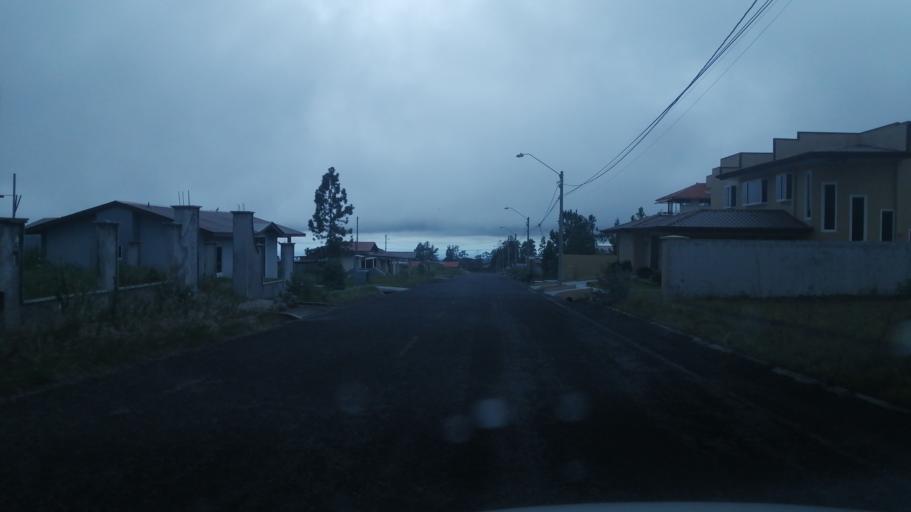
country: PA
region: Chiriqui
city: Palmira
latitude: 8.7192
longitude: -82.4411
